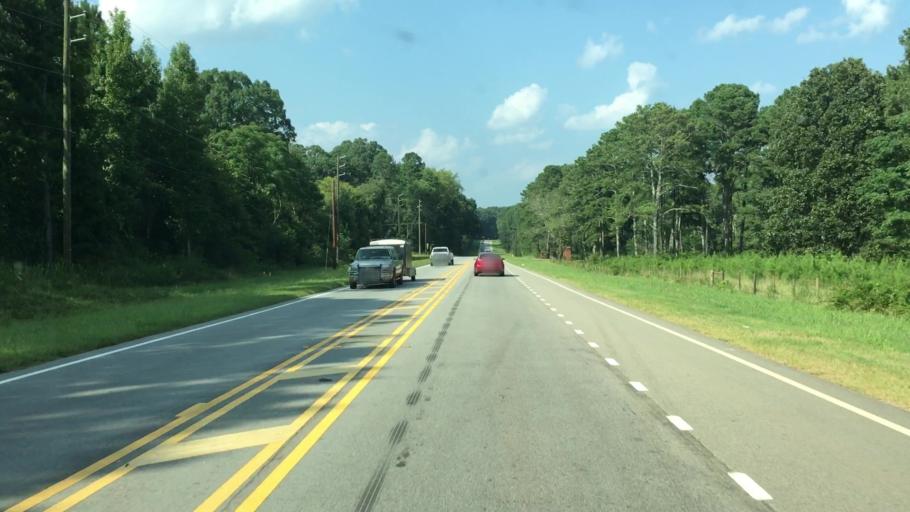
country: US
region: Georgia
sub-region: Walton County
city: Social Circle
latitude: 33.6167
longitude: -83.7481
